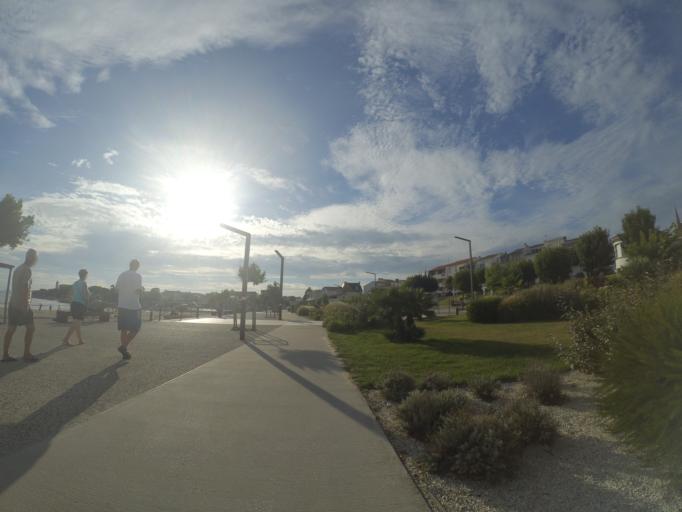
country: FR
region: Poitou-Charentes
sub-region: Departement de la Charente-Maritime
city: Saint-Georges-de-Didonne
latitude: 45.6010
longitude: -0.9980
